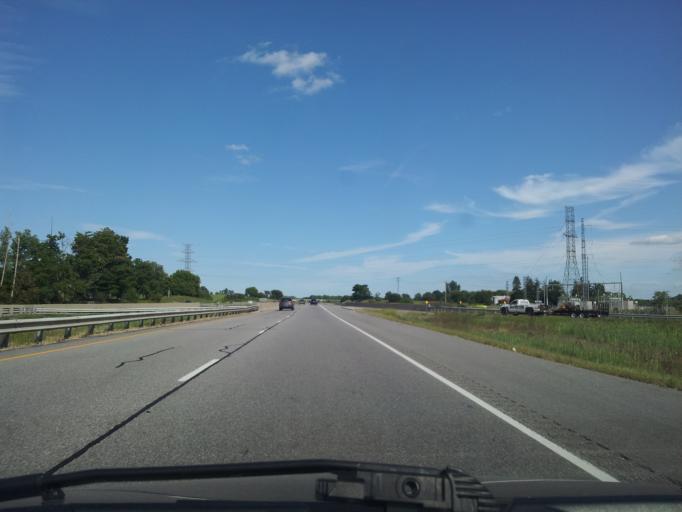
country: CA
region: Ontario
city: Kitchener
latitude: 43.3932
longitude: -80.6575
